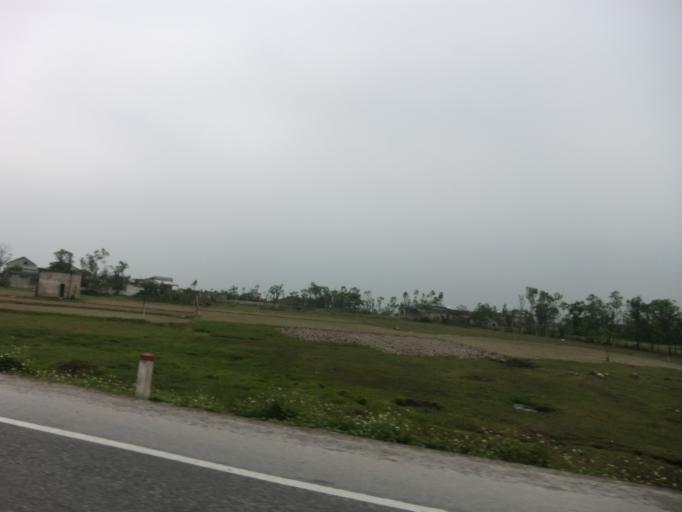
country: VN
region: Ha Tinh
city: Ky Anh
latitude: 18.0245
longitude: 106.3637
